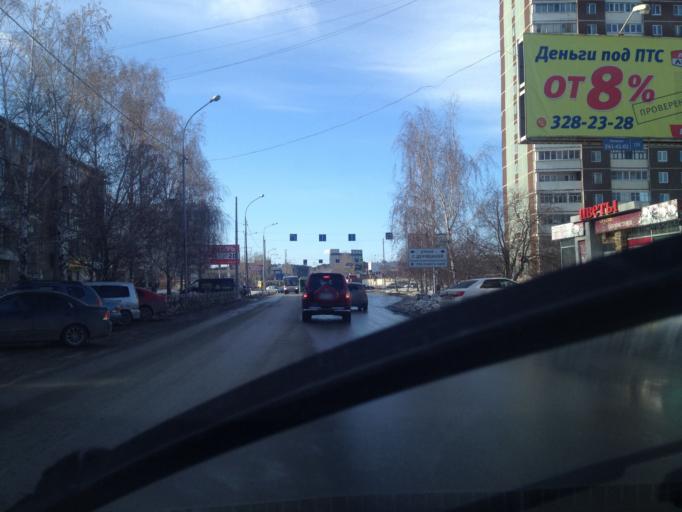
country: RU
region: Sverdlovsk
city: Sovkhoznyy
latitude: 56.8093
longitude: 60.5485
